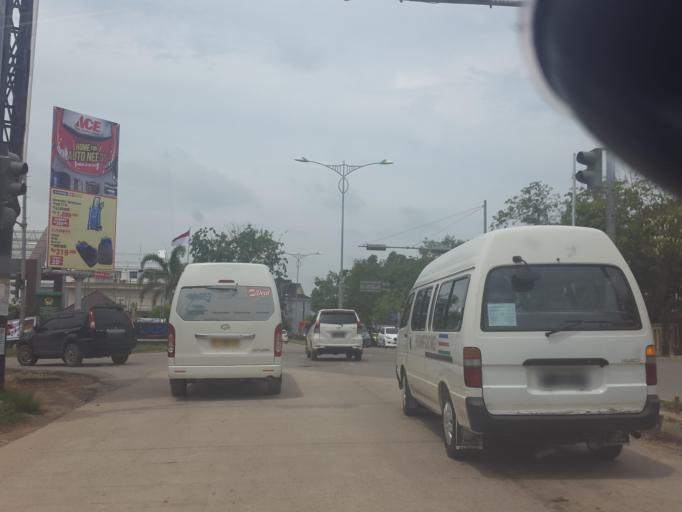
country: SG
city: Singapore
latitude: 1.1281
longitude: 104.0573
